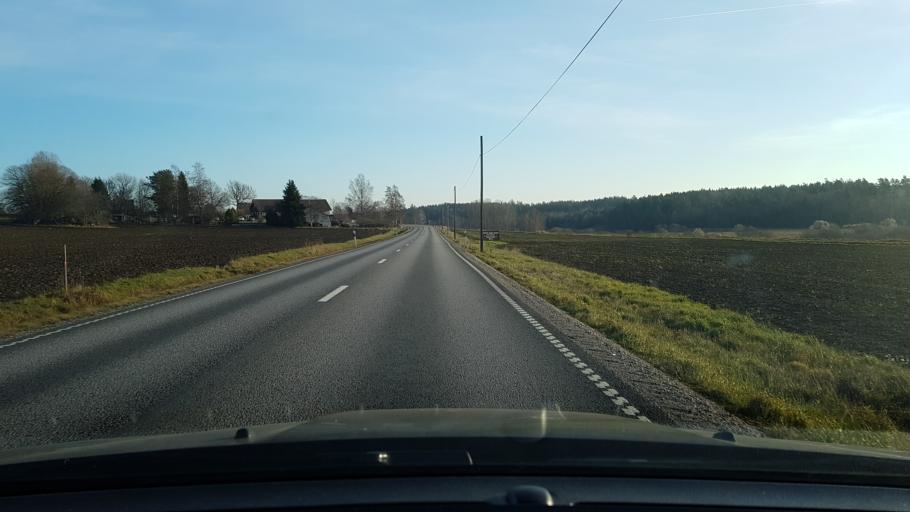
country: SE
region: Stockholm
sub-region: Norrtalje Kommun
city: Nykvarn
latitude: 59.7368
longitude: 18.2454
